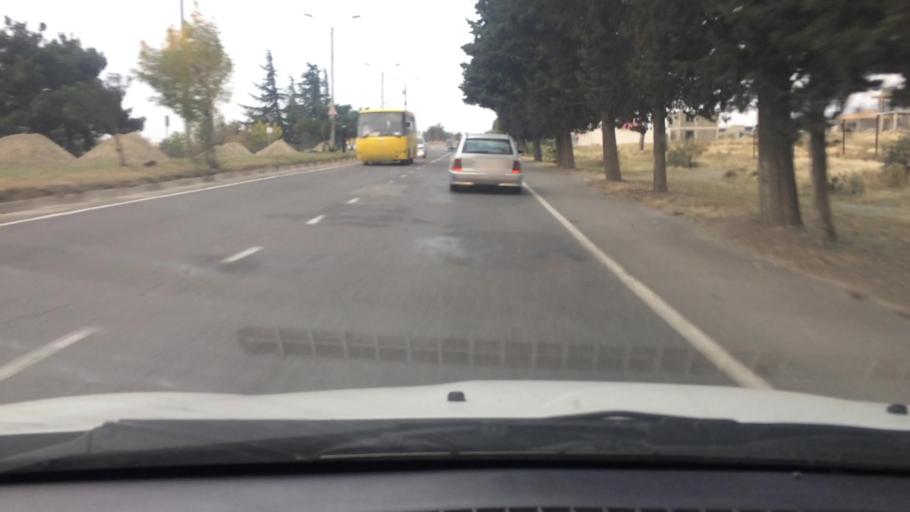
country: GE
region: T'bilisi
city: Tbilisi
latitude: 41.6447
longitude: 44.8942
